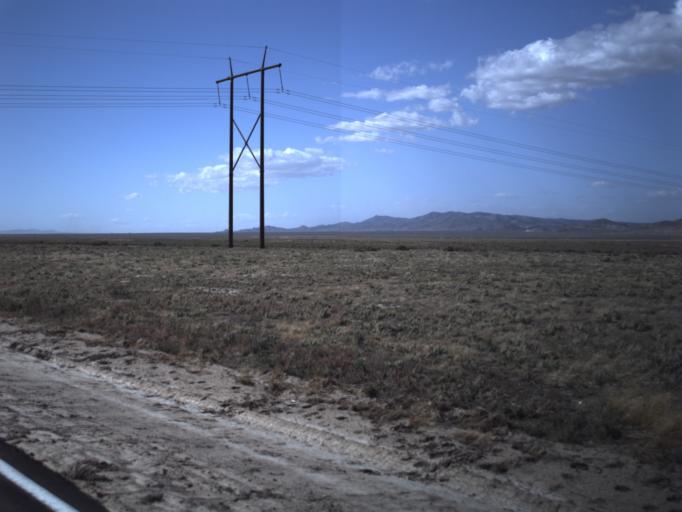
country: US
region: Utah
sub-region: Beaver County
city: Milford
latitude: 38.4894
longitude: -112.9911
